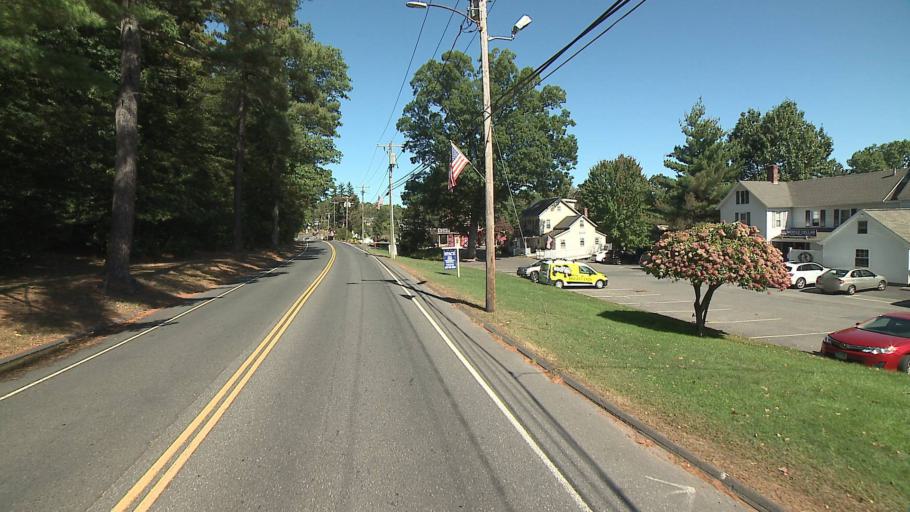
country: US
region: Connecticut
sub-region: Hartford County
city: Simsbury Center
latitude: 41.8607
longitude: -72.8103
